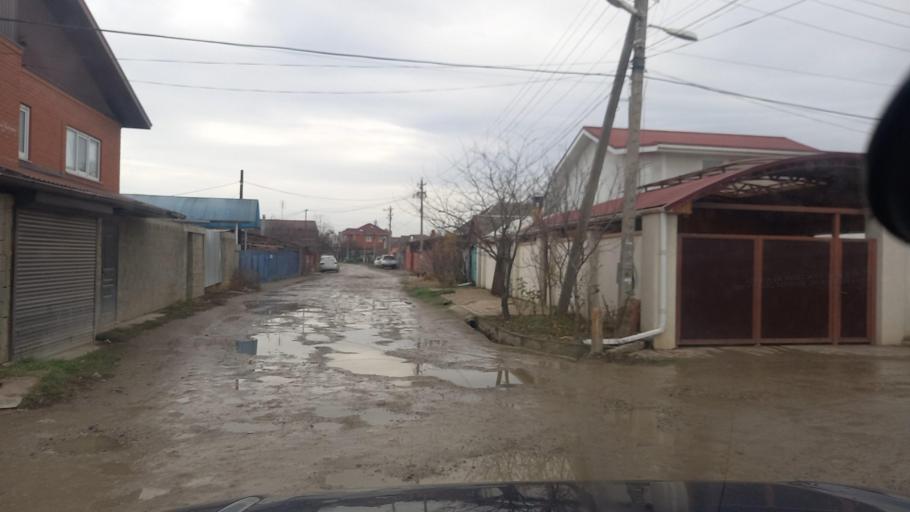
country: RU
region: Adygeya
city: Yablonovskiy
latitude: 44.9851
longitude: 38.9455
